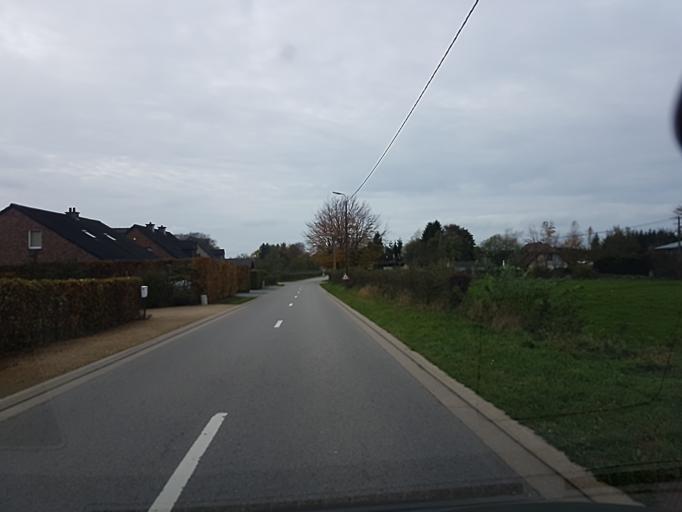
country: BE
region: Wallonia
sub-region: Province de Liege
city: Malmedy
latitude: 50.4805
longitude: 5.9957
